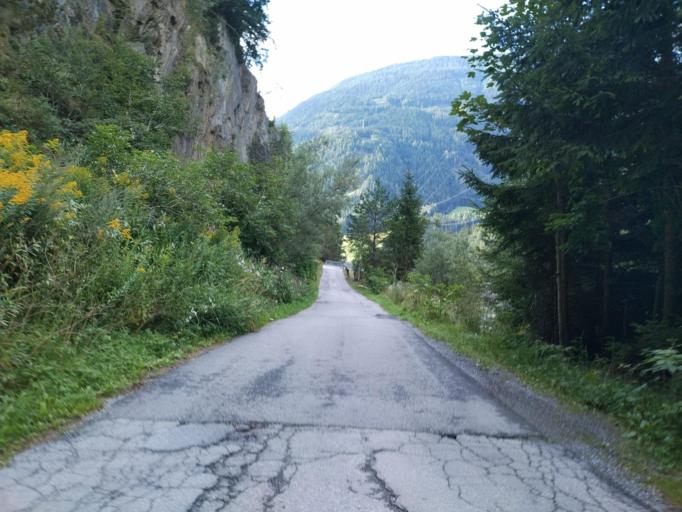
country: AT
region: Tyrol
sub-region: Politischer Bezirk Lienz
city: Hopfgarten in Defereggen
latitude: 46.9351
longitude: 12.5762
